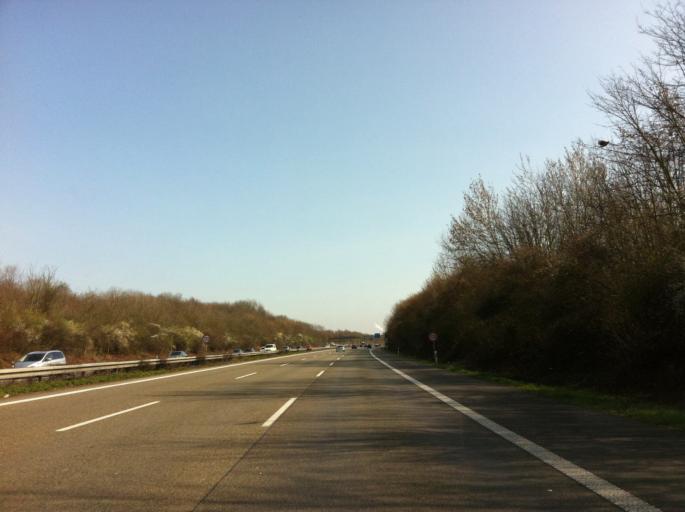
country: DE
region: North Rhine-Westphalia
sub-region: Regierungsbezirk Koln
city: Bilderstoeckchen
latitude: 51.0120
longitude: 6.9173
